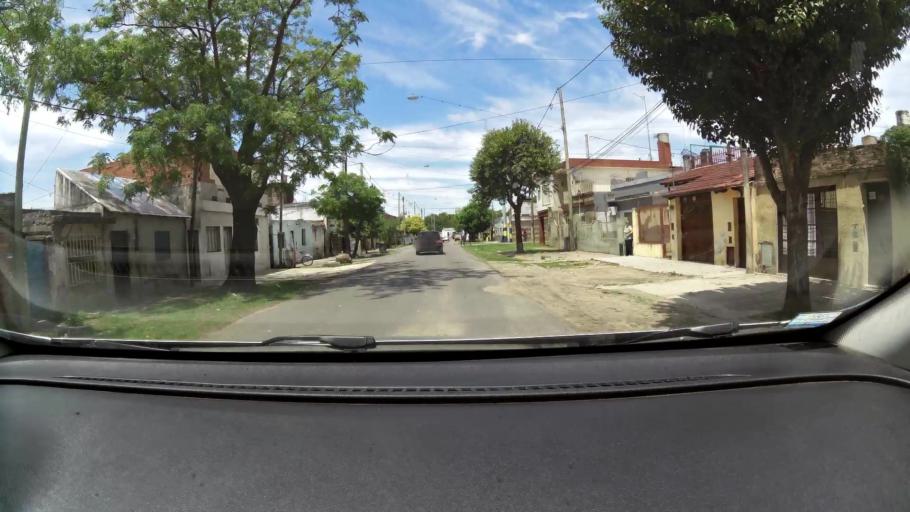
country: AR
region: Santa Fe
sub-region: Departamento de Rosario
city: Rosario
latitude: -32.9864
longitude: -60.6255
